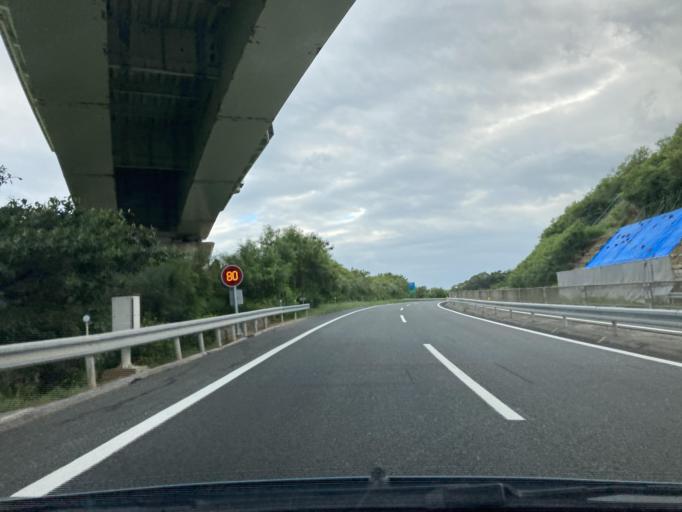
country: JP
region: Okinawa
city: Ginowan
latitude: 26.2179
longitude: 127.7395
